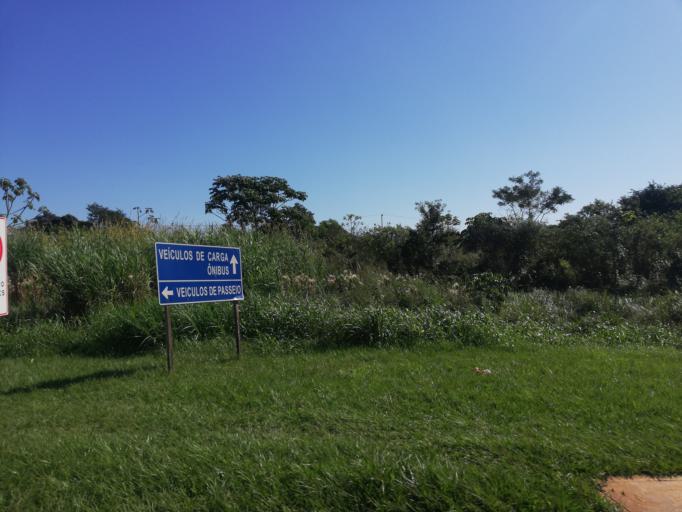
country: AR
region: Misiones
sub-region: Departamento de Iguazu
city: Puerto Iguazu
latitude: -25.5776
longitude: -54.5564
